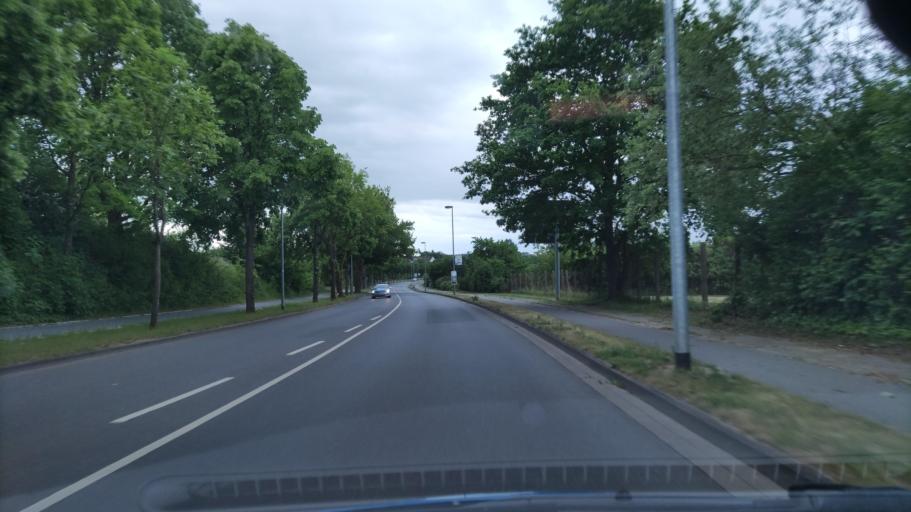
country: DE
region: Mecklenburg-Vorpommern
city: Parchim
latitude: 53.4309
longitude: 11.8644
